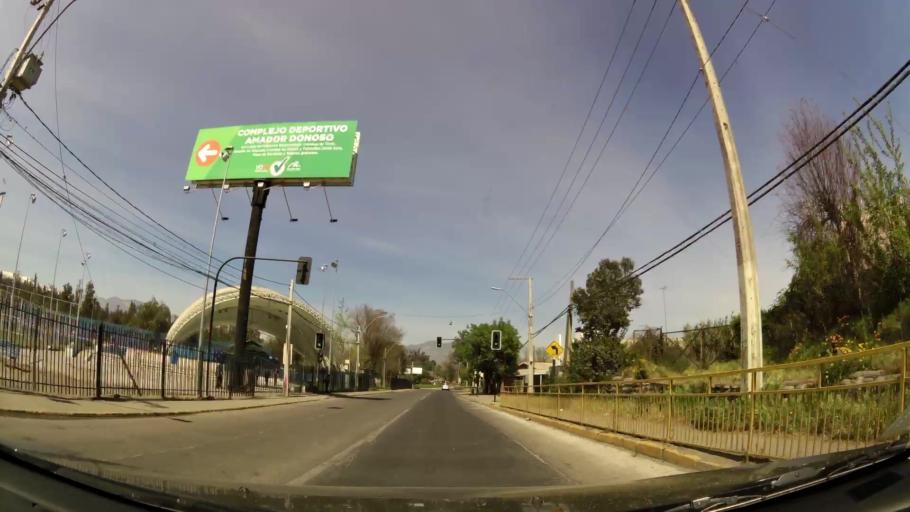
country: CL
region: Santiago Metropolitan
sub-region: Provincia de Cordillera
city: Puente Alto
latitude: -33.6247
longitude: -70.5756
